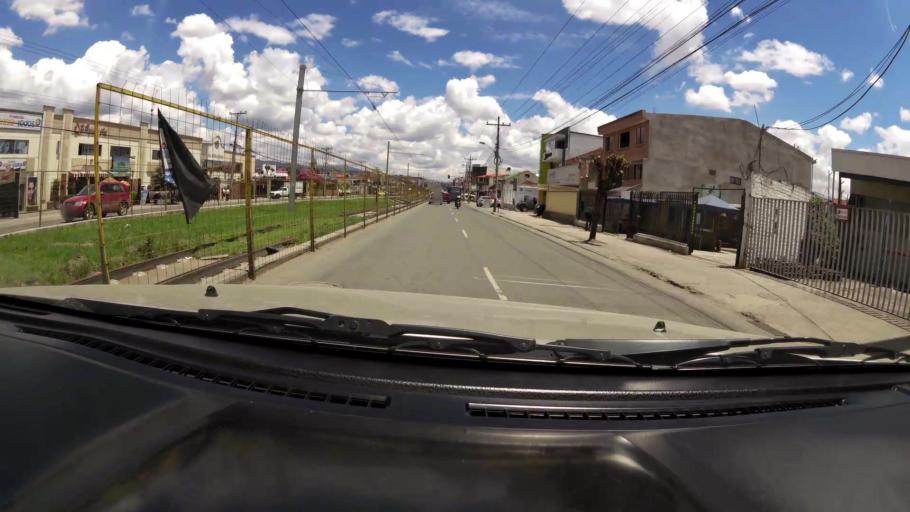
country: EC
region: Azuay
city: Cuenca
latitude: -2.9162
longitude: -79.0387
